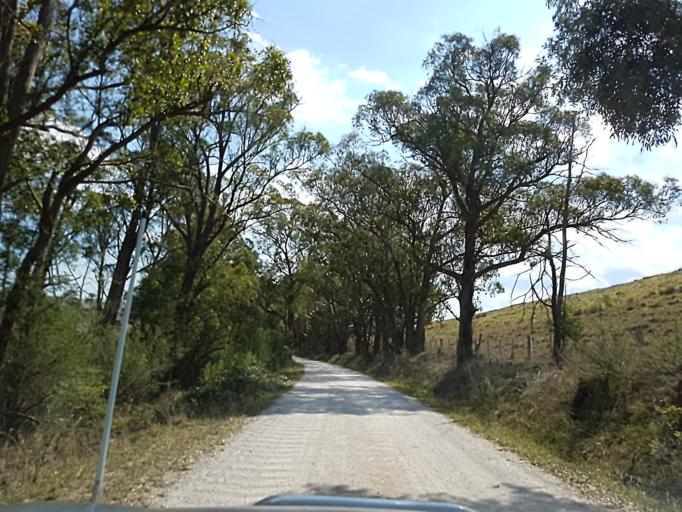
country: AU
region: Victoria
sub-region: East Gippsland
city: Lakes Entrance
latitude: -37.4978
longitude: 148.2252
